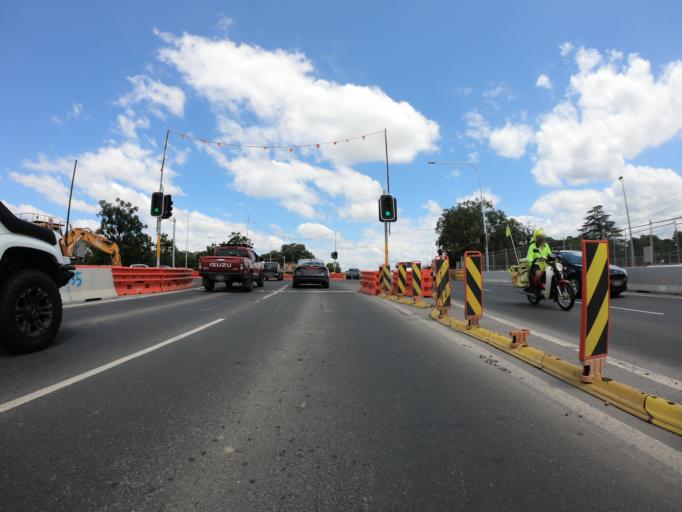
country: AU
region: New South Wales
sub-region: Penrith Municipality
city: Penrith
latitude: -33.7491
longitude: 150.6883
